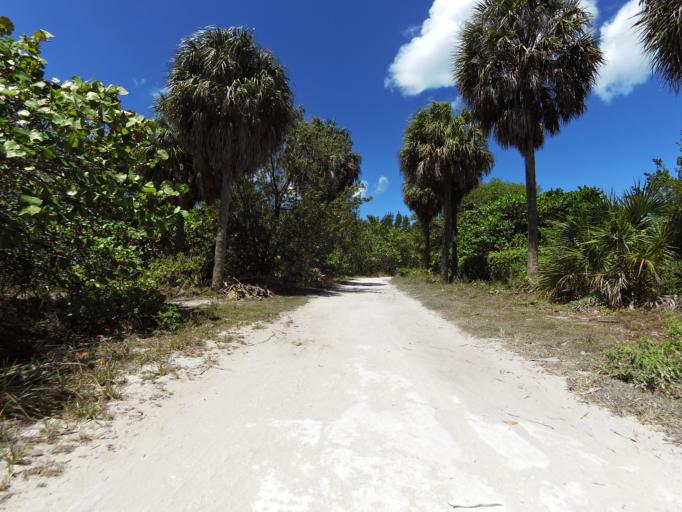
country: US
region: Florida
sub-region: Miami-Dade County
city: Key Biscayne
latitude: 25.6657
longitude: -80.1583
